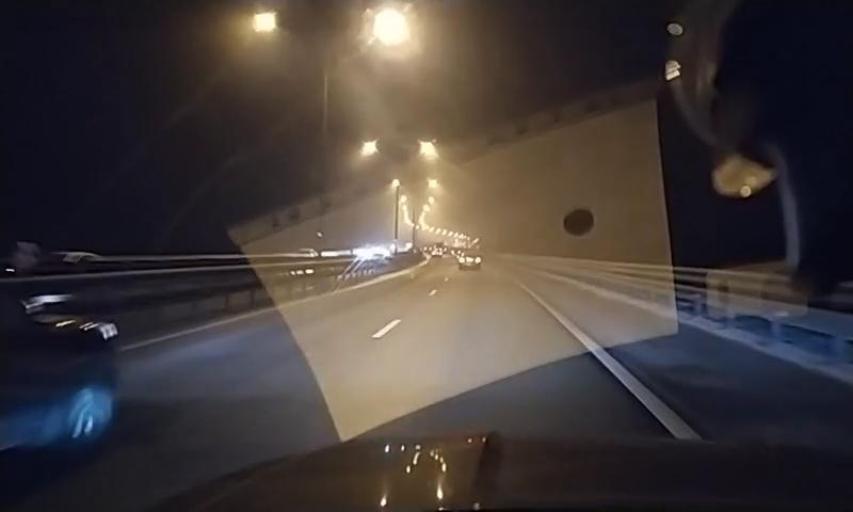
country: RU
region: Leningrad
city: Bugry
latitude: 60.1101
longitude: 30.3875
